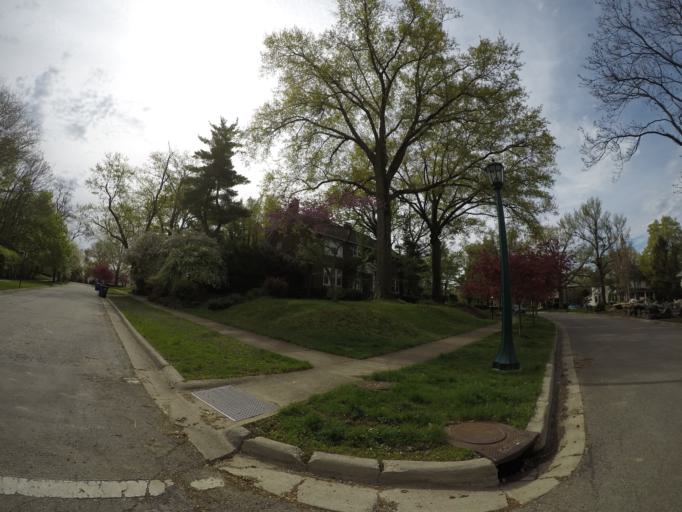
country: US
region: Ohio
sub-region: Franklin County
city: Upper Arlington
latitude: 39.9924
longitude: -83.0632
